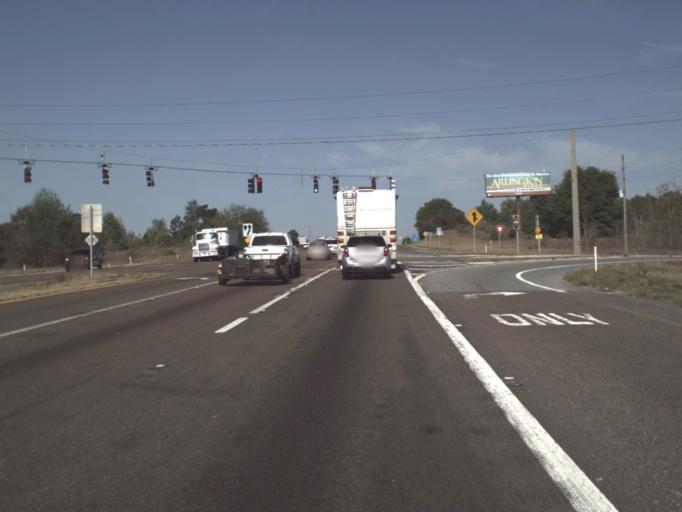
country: US
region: Florida
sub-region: Lake County
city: Howie In The Hills
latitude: 28.6430
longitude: -81.8085
